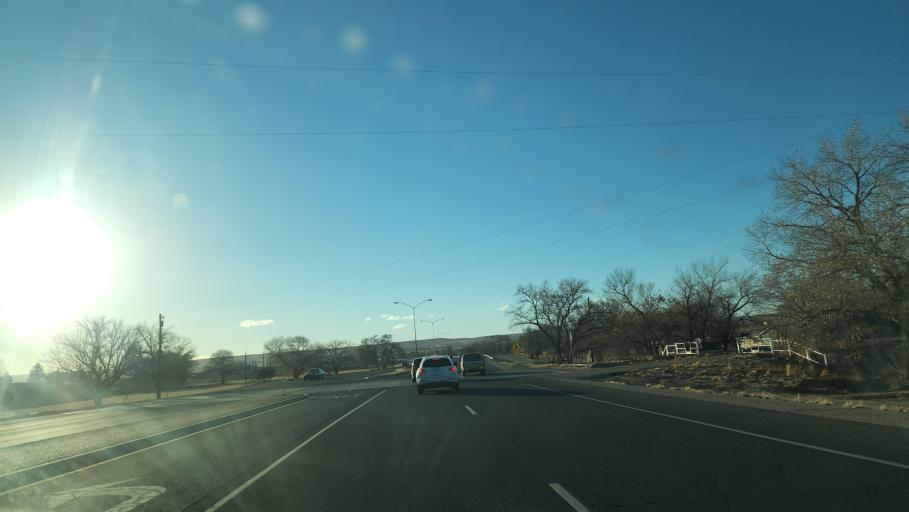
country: US
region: New Mexico
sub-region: Bernalillo County
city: South Valley
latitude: 35.0271
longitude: -106.7041
